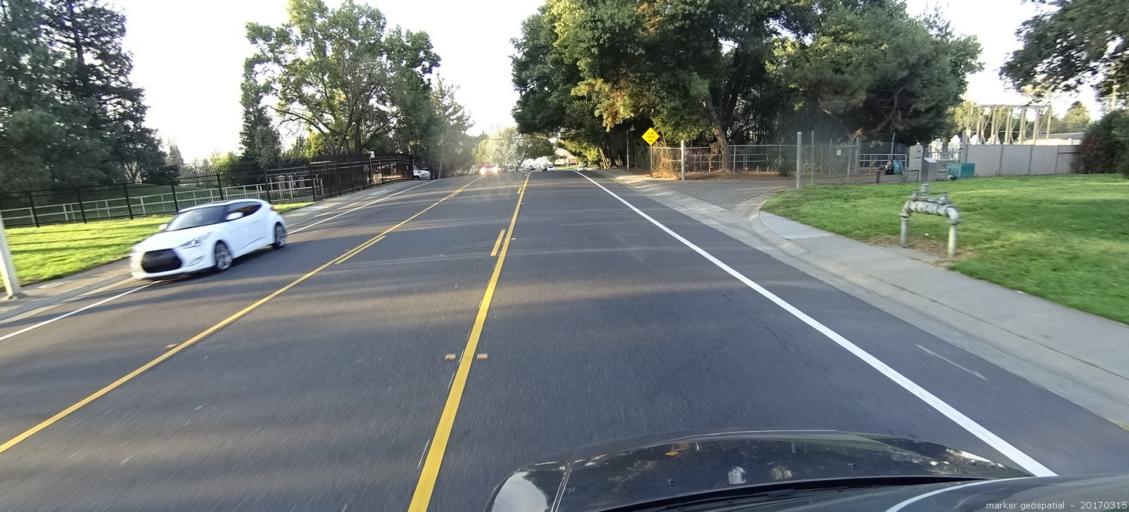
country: US
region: California
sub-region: Sacramento County
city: Parkway
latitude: 38.5234
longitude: -121.5116
